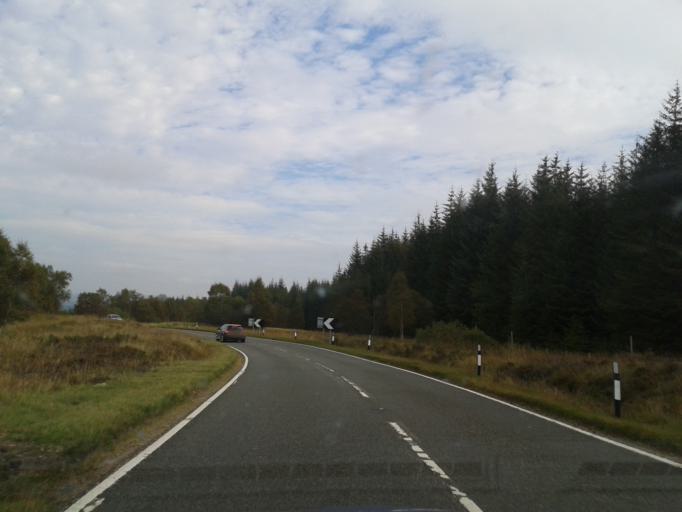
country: GB
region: Scotland
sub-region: Highland
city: Spean Bridge
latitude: 57.1319
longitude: -4.9589
